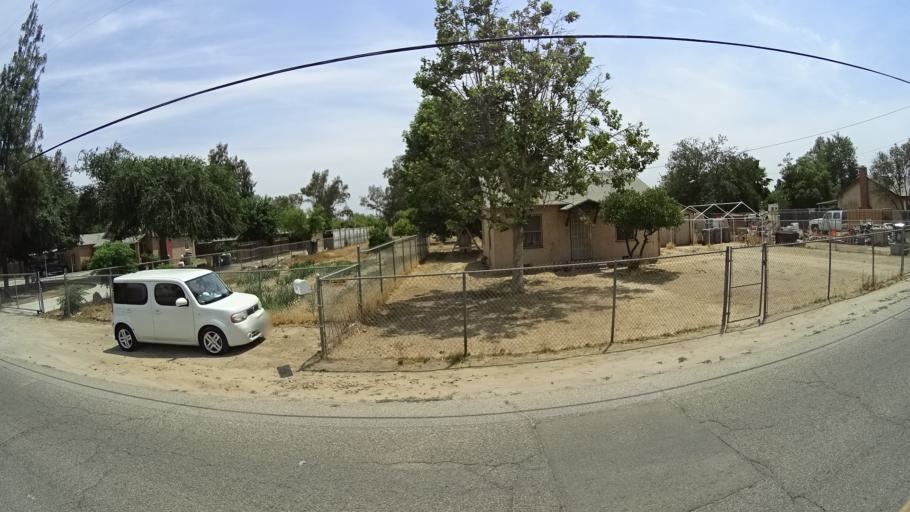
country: US
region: California
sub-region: Fresno County
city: West Park
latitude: 36.7591
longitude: -119.8533
